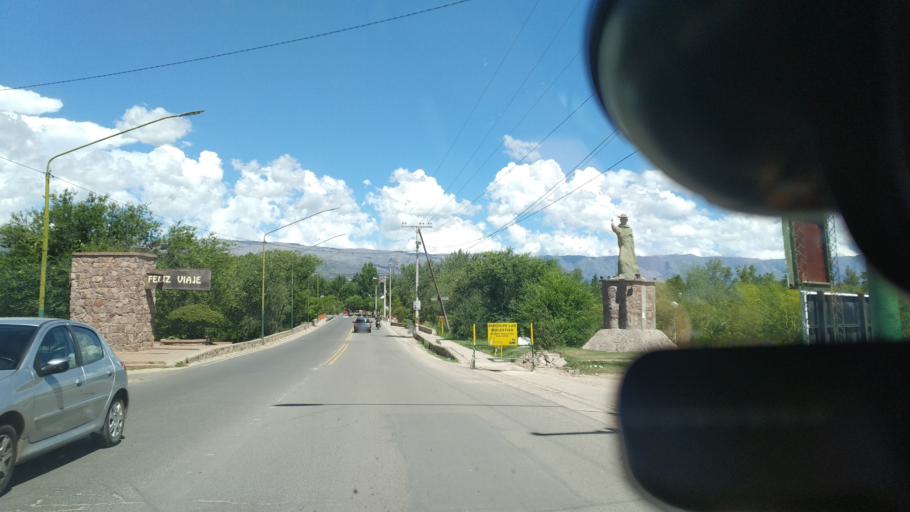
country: AR
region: Cordoba
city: Mina Clavero
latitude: -31.7190
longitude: -65.0102
